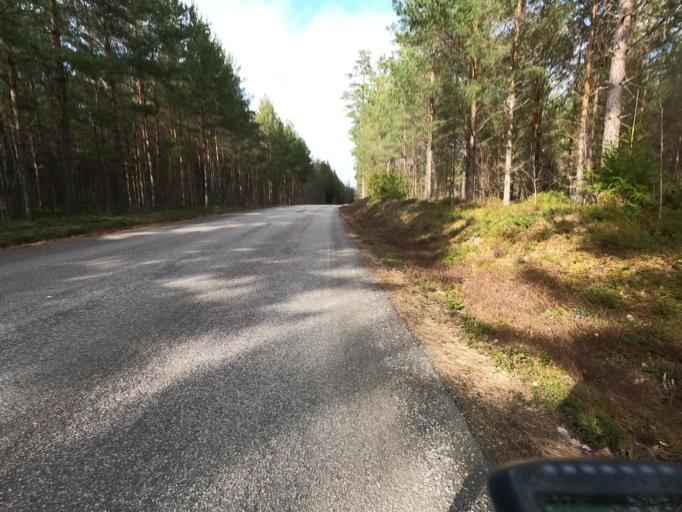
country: SE
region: Kronoberg
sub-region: Alvesta Kommun
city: Vislanda
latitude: 56.8031
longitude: 14.4882
